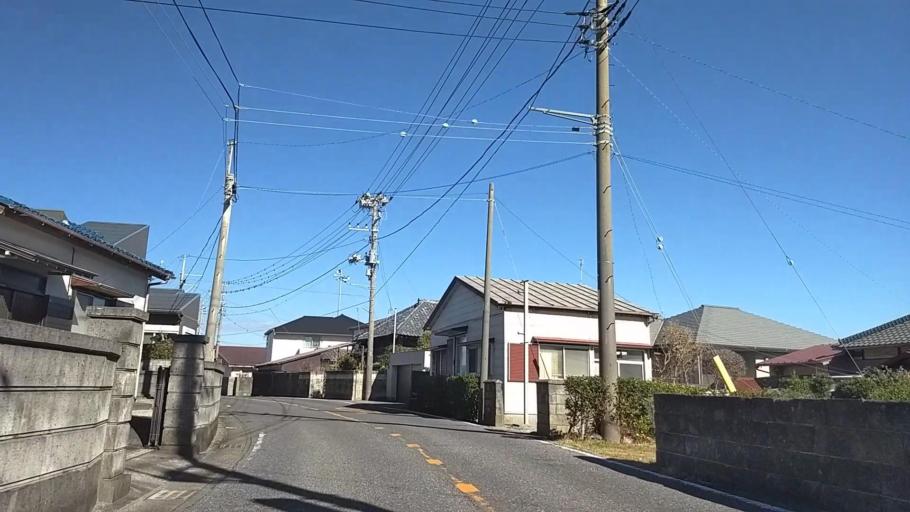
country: JP
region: Chiba
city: Tateyama
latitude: 34.9463
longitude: 139.9628
